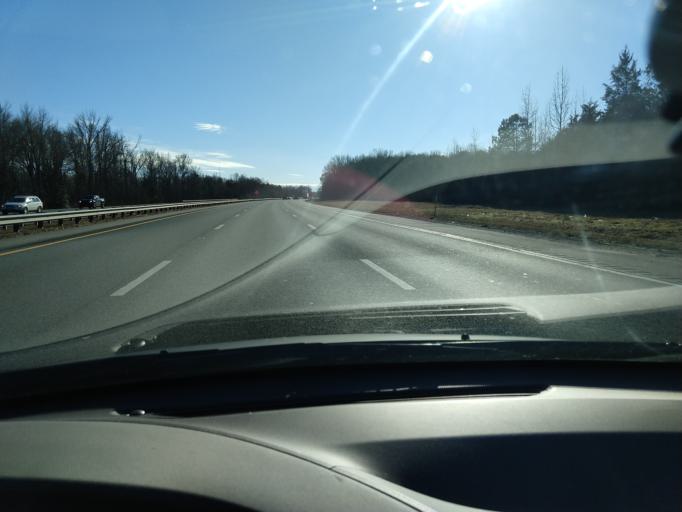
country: US
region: Virginia
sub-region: Spotsylvania County
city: Spotsylvania Courthouse
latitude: 38.1447
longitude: -77.5062
